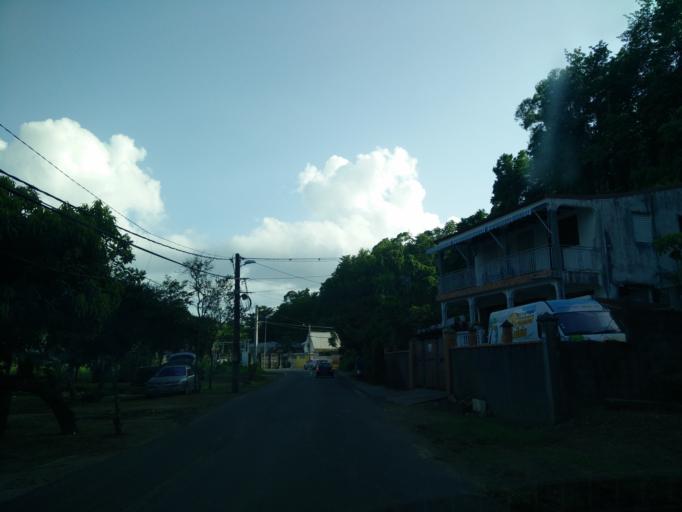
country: GP
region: Guadeloupe
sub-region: Guadeloupe
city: Pointe-a-Pitre
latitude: 16.2375
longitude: -61.5123
